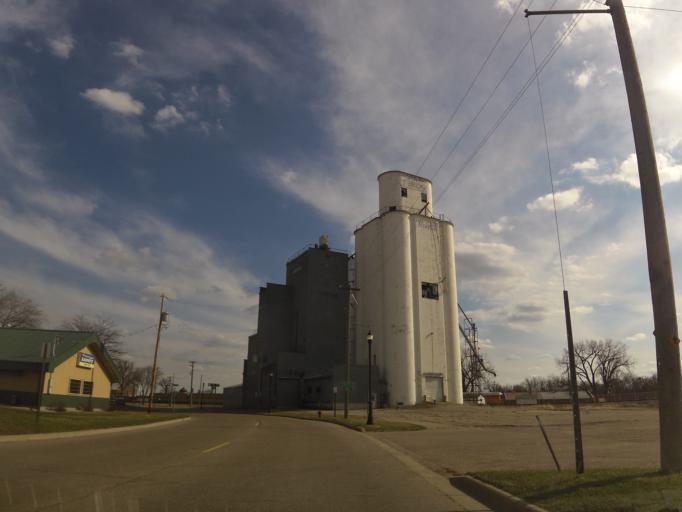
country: US
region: Minnesota
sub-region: Chippewa County
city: Montevideo
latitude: 44.9437
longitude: -95.7261
